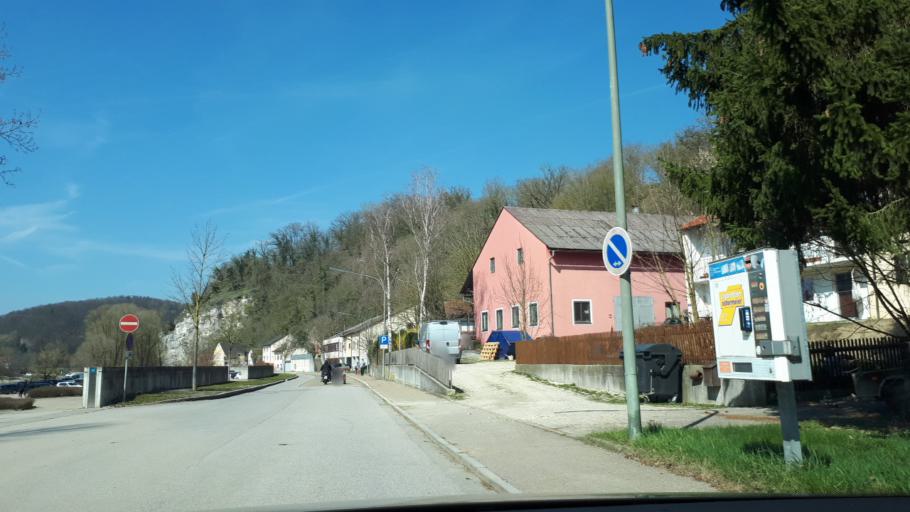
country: DE
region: Bavaria
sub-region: Lower Bavaria
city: Essing
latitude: 48.8917
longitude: 11.8250
